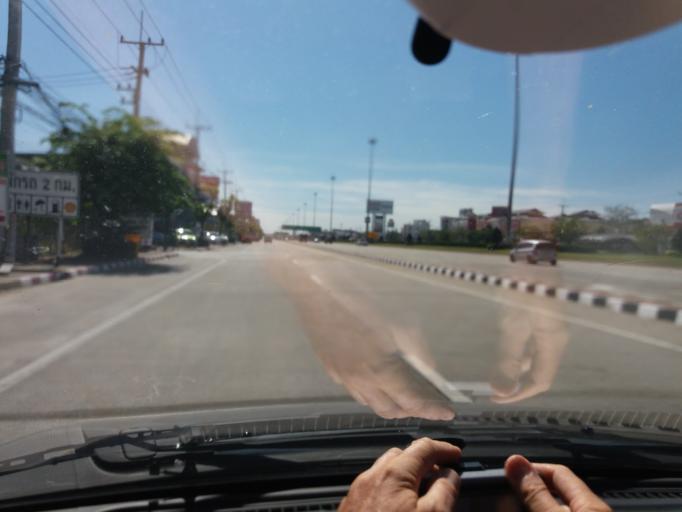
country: TH
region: Suphan Buri
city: Suphan Buri
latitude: 14.4743
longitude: 100.1318
